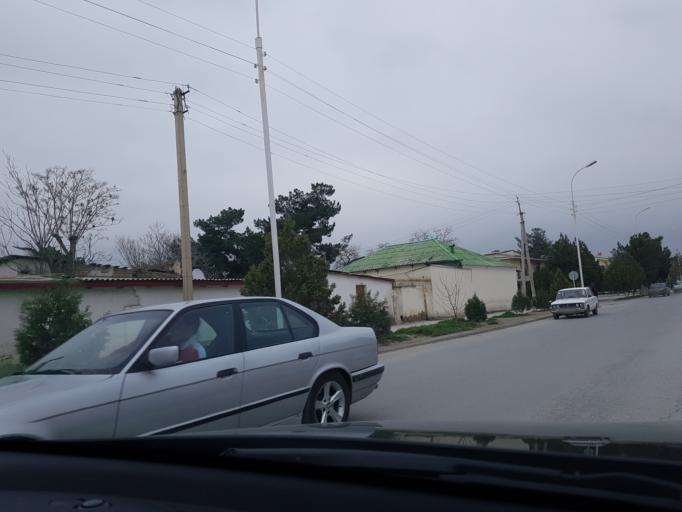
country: TM
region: Ahal
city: Abadan
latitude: 38.1571
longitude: 57.9613
